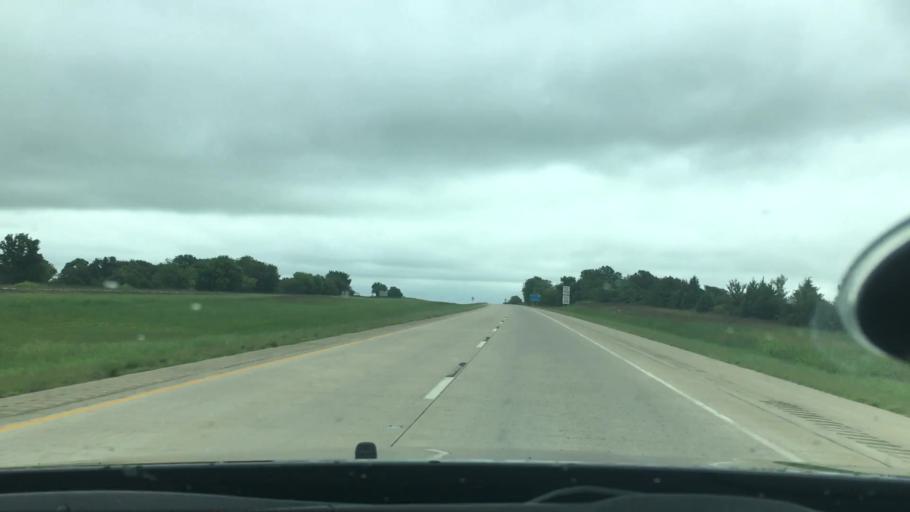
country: US
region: Oklahoma
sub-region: McIntosh County
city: Checotah
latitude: 35.4569
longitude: -95.5829
